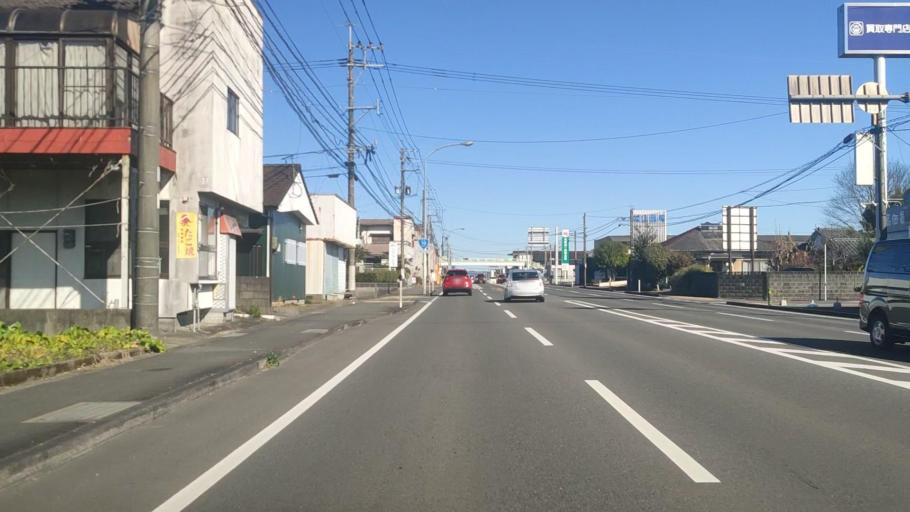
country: JP
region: Miyazaki
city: Miyakonojo
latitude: 31.7409
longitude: 131.0724
